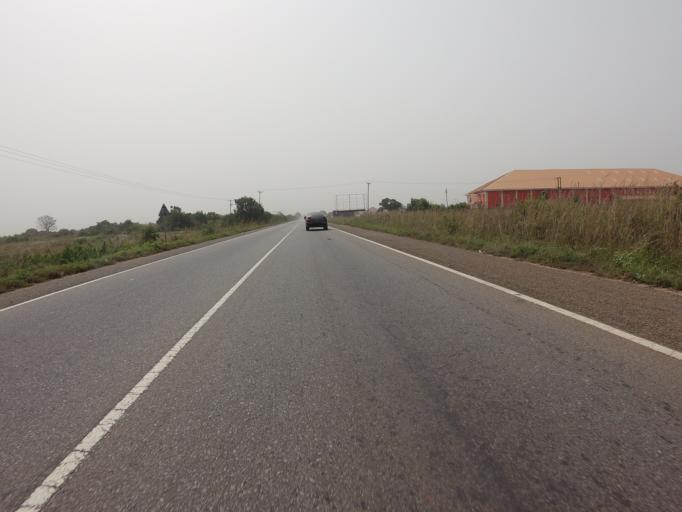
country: GH
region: Volta
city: Anloga
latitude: 5.9304
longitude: 0.5233
